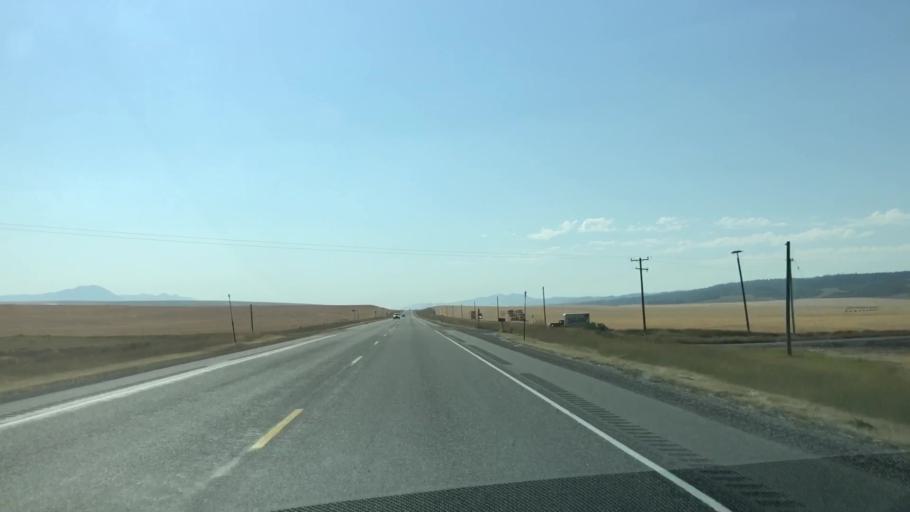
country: US
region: Idaho
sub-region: Madison County
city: Rexburg
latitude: 43.5501
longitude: -111.5298
